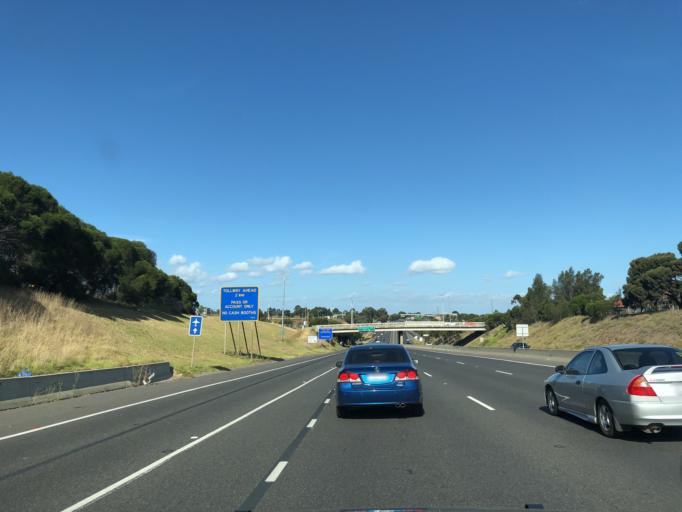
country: AU
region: Victoria
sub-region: Moonee Valley
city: Keilor East
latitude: -37.7287
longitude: 144.8668
